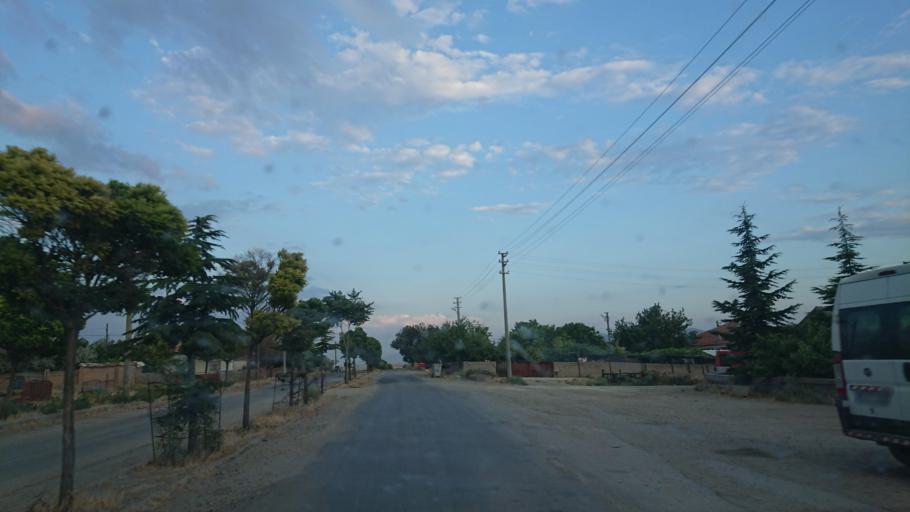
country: TR
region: Aksaray
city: Agacoren
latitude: 38.9219
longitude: 34.0347
